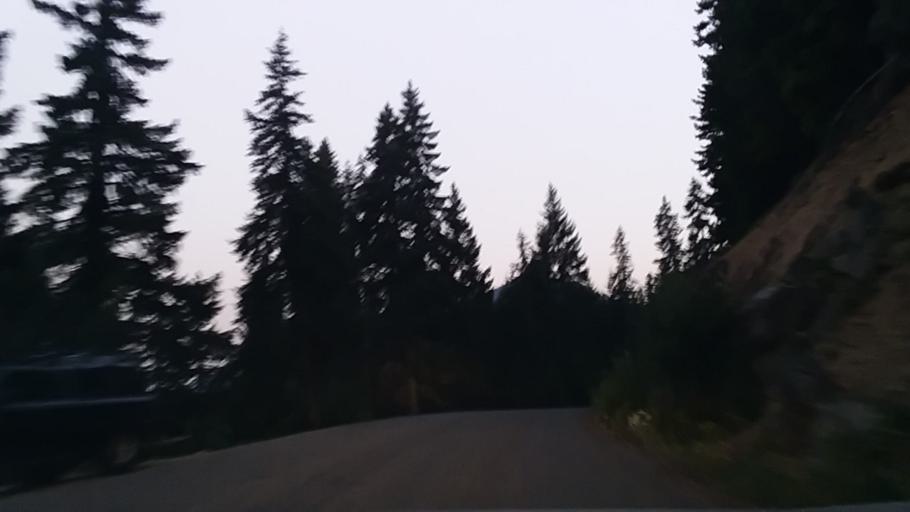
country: US
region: Washington
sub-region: Kittitas County
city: Cle Elum
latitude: 47.3392
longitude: -121.2540
